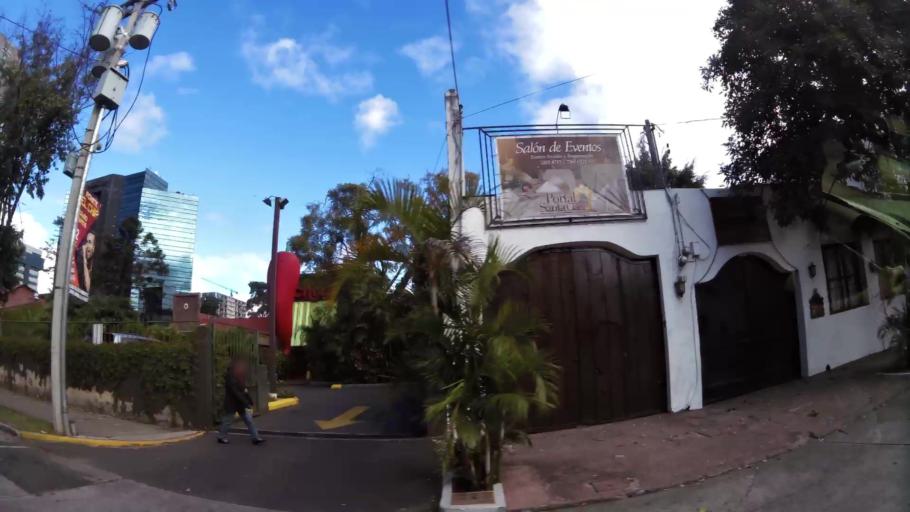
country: GT
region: Guatemala
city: Santa Catarina Pinula
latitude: 14.5977
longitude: -90.5123
